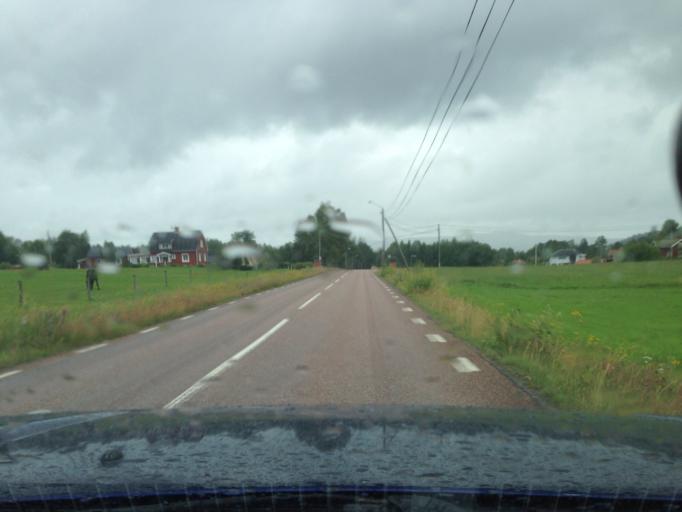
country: SE
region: Dalarna
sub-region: Ludvika Kommun
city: Grangesberg
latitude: 60.1404
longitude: 14.9972
